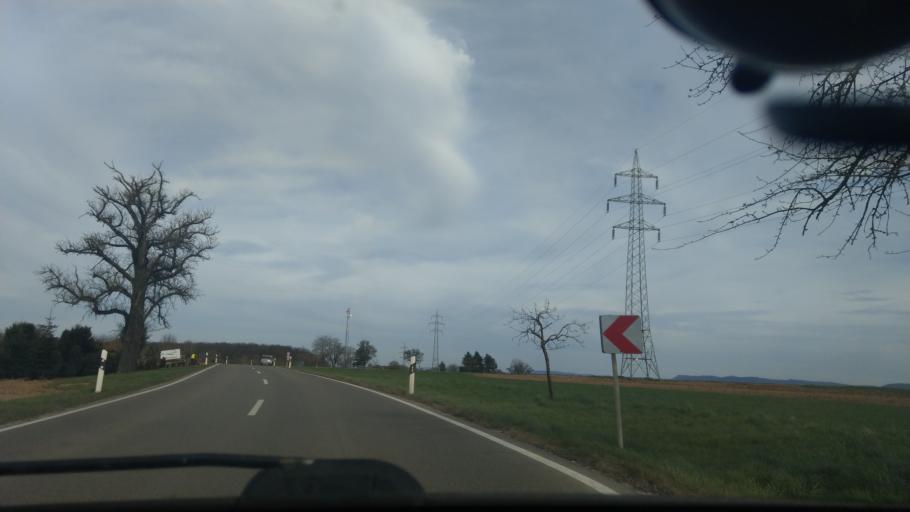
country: DE
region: Baden-Wuerttemberg
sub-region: Regierungsbezirk Stuttgart
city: Wolfschlugen
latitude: 48.6646
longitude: 9.2626
